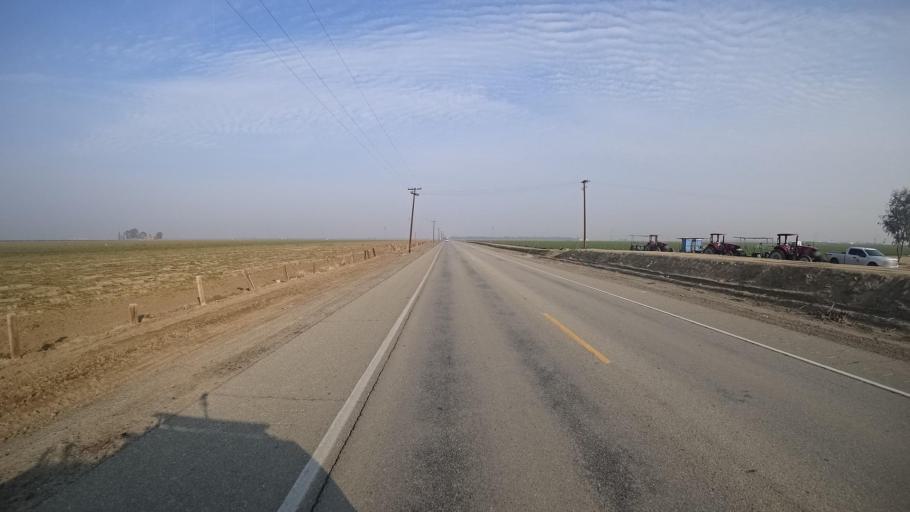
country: US
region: California
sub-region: Kern County
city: Weedpatch
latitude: 35.1144
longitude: -118.9147
